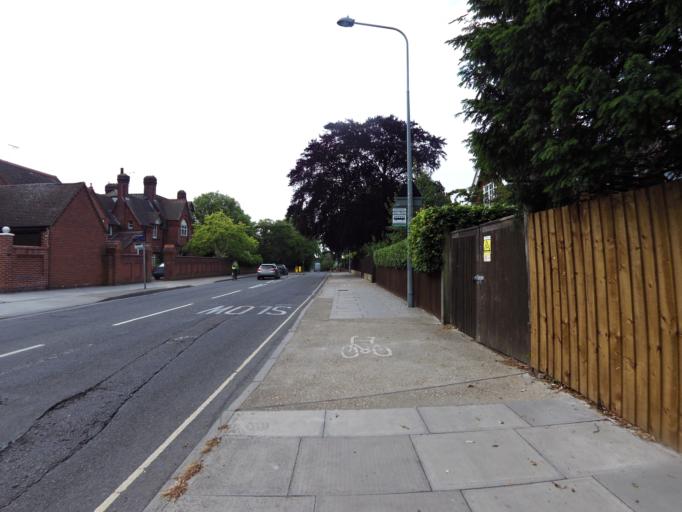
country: GB
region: England
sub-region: Suffolk
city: Ipswich
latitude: 52.0684
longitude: 1.1537
